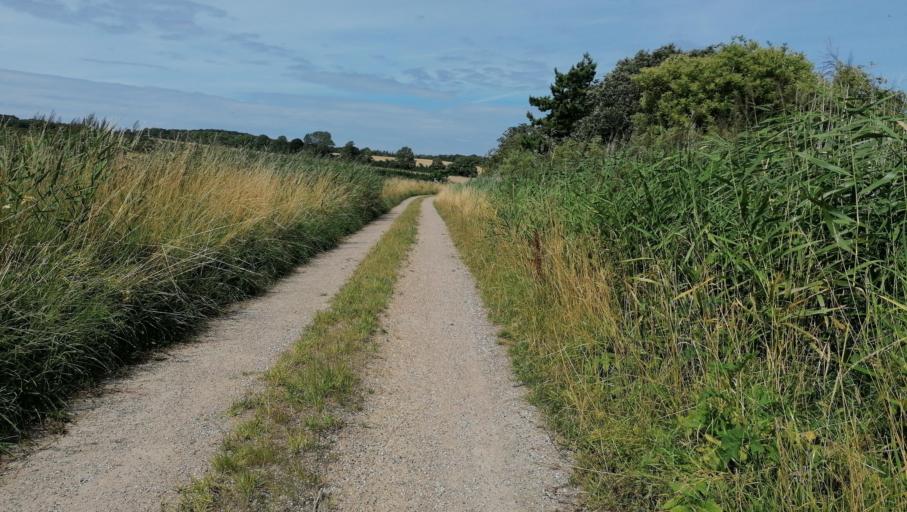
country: DK
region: Zealand
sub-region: Odsherred Kommune
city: Horve
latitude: 55.7806
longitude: 11.4193
